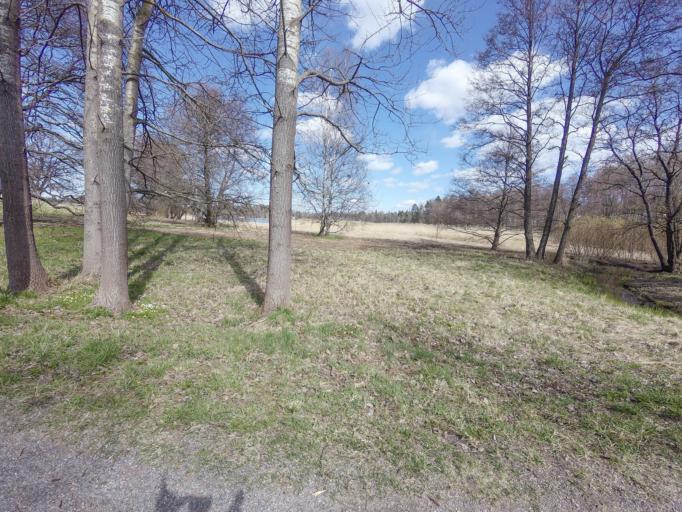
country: FI
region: Uusimaa
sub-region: Helsinki
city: Helsinki
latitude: 60.1793
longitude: 25.0367
